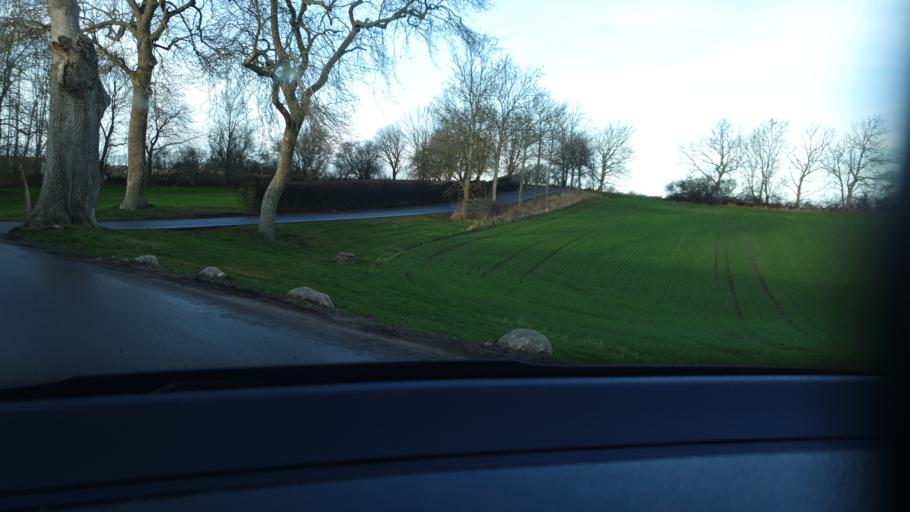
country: DK
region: Zealand
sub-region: Odsherred Kommune
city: Nykobing Sjaelland
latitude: 55.9230
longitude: 11.6379
